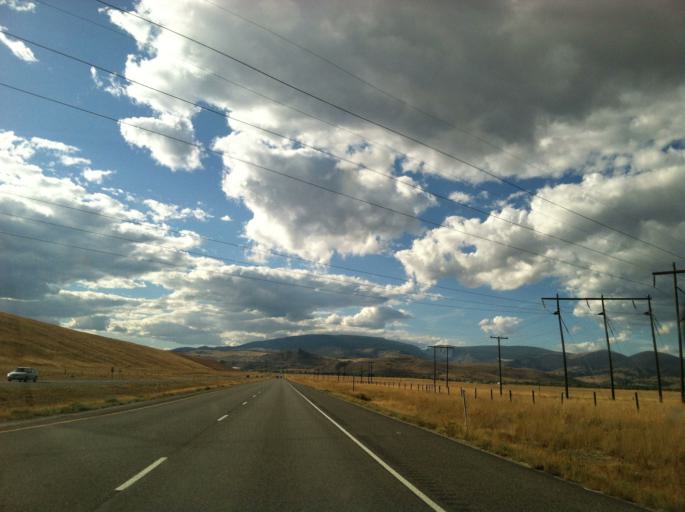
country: US
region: Montana
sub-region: Deer Lodge County
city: Anaconda
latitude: 46.1193
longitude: -112.8760
